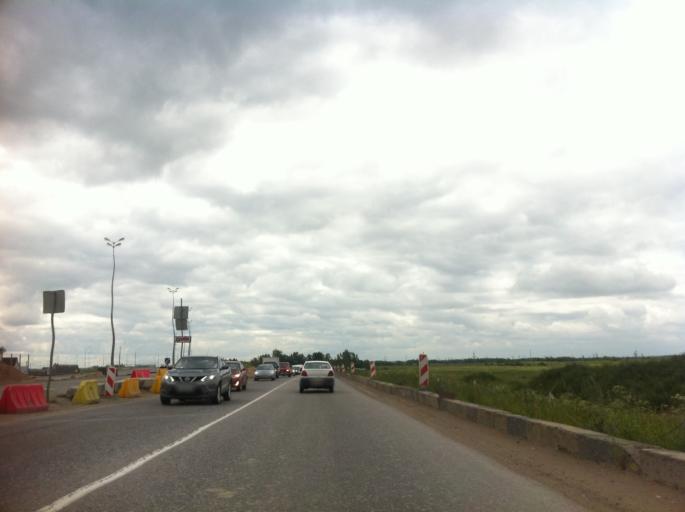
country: RU
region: Leningrad
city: Maloye Verevo
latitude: 59.6701
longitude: 30.2315
